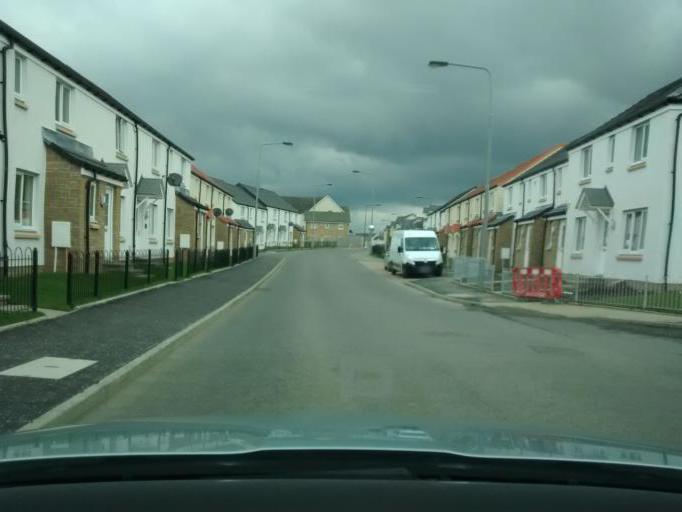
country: GB
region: Scotland
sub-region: West Lothian
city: Bathgate
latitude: 55.8905
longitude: -3.6478
